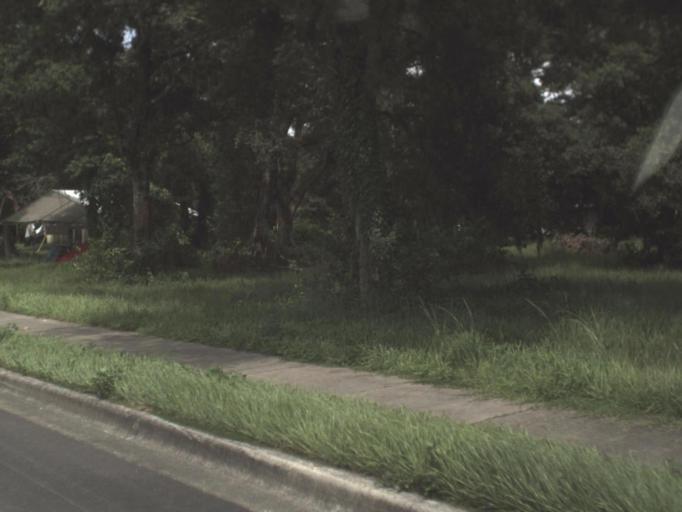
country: US
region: Florida
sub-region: Hernando County
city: Masaryktown
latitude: 28.4779
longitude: -82.4369
